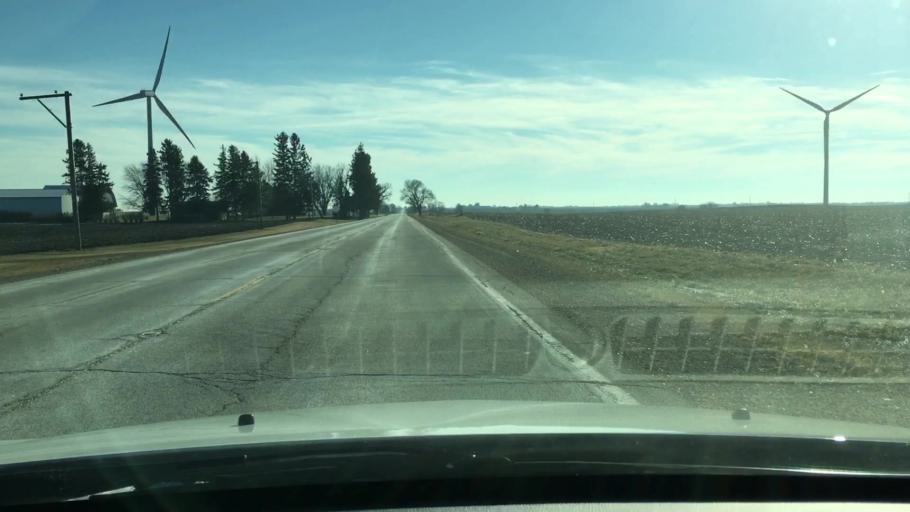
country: US
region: Illinois
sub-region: LaSalle County
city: Mendota
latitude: 41.6262
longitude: -89.1291
